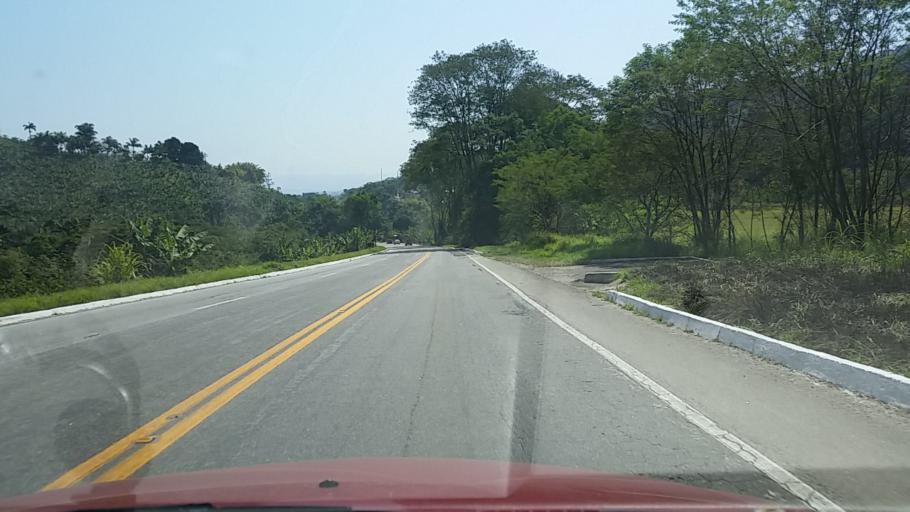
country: BR
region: Sao Paulo
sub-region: Miracatu
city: Miracatu
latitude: -24.3440
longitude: -47.4979
